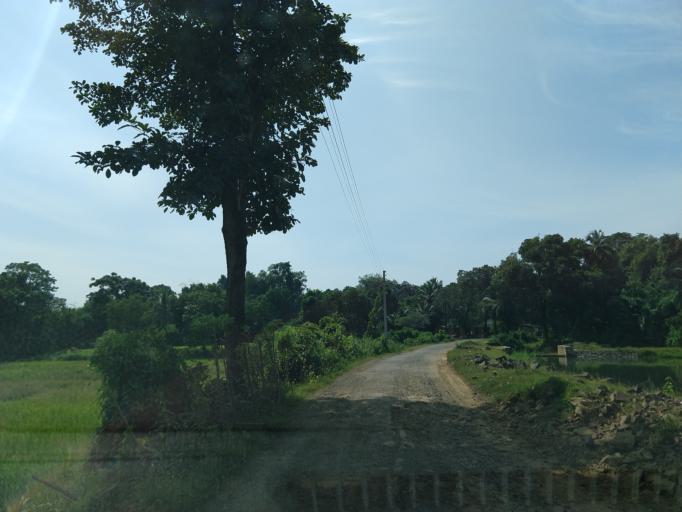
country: IN
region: Maharashtra
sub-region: Sindhudurg
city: Kudal
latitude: 16.0438
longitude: 73.6842
